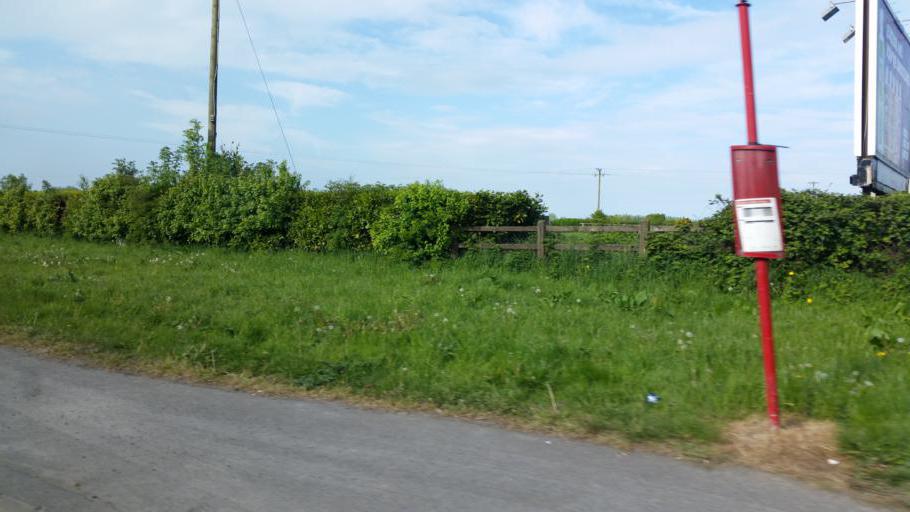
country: IE
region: Leinster
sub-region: Dublin City
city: Finglas
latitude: 53.4336
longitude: -6.3332
